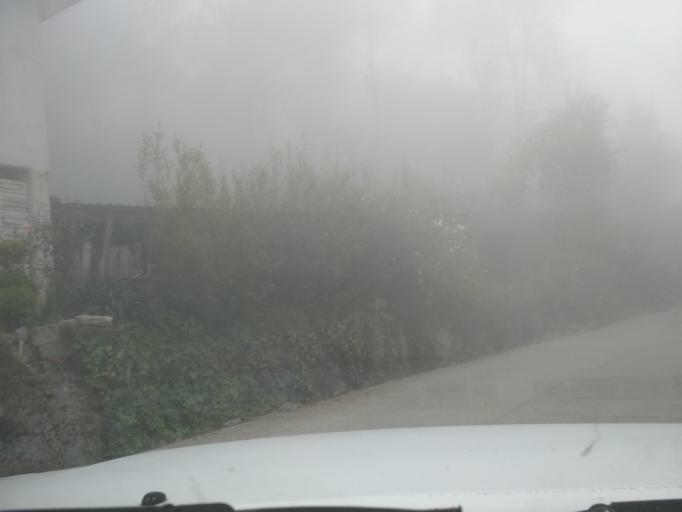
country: MX
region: Veracruz
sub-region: La Perla
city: Chilapa
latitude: 18.9790
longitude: -97.1886
